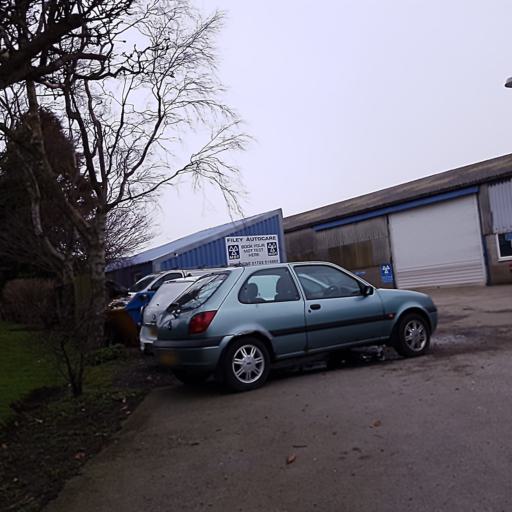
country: GB
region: England
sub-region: North Yorkshire
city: Filey
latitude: 54.2110
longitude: -0.2942
